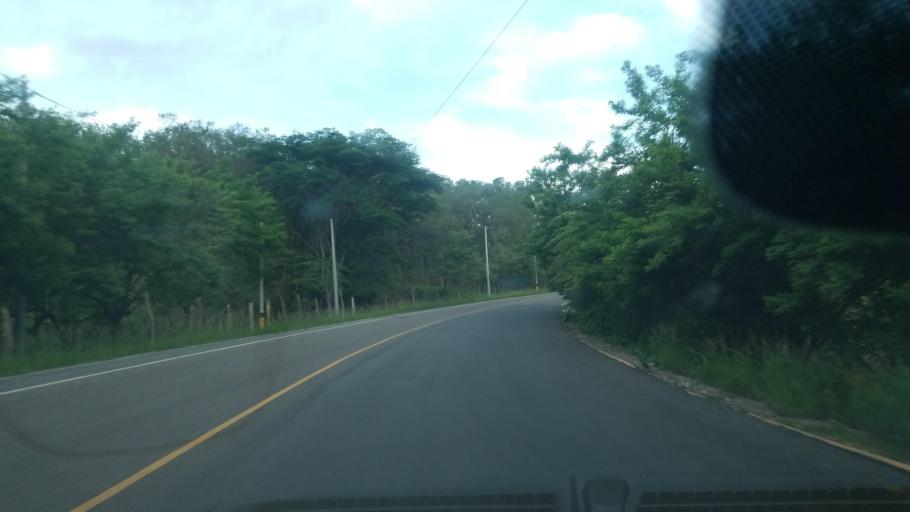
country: HN
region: Santa Barbara
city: Concepcion del Sur
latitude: 14.8001
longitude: -88.1704
